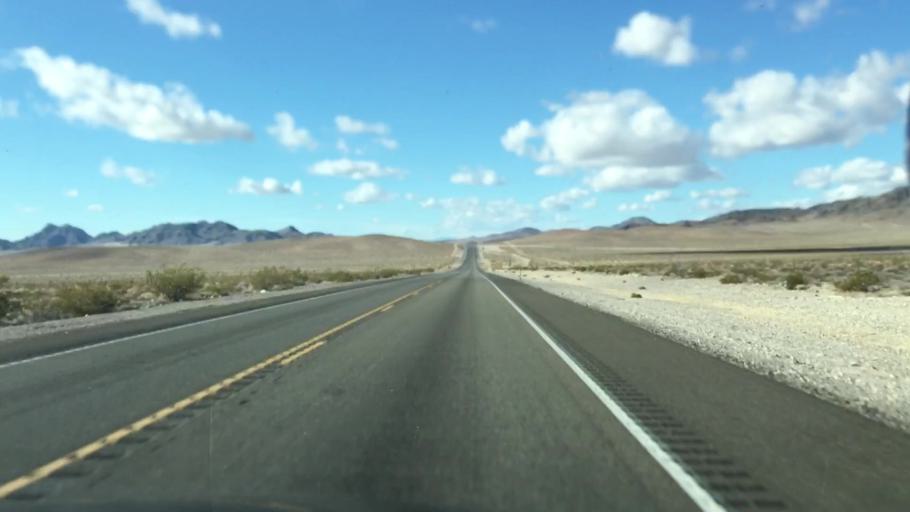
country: US
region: Nevada
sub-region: Nye County
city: Pahrump
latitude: 36.6055
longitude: -116.2588
